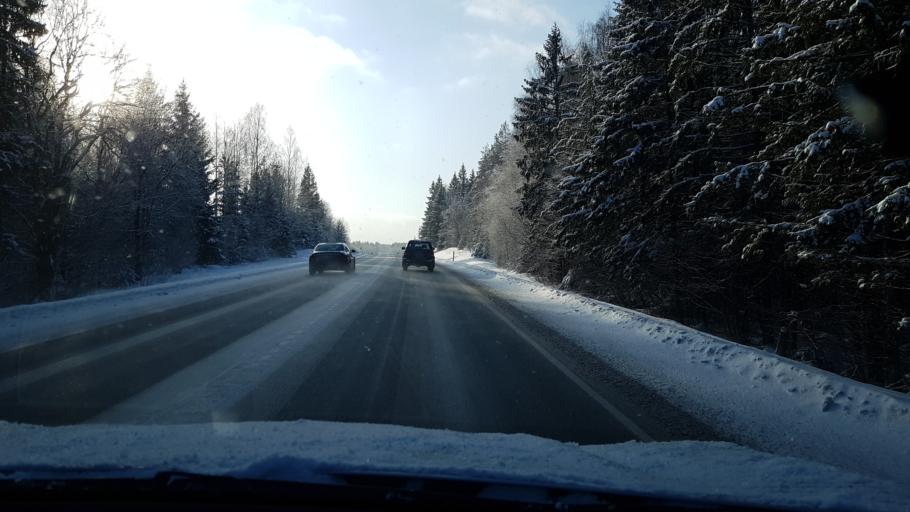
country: EE
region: Harju
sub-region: Keila linn
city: Keila
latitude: 59.2210
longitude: 24.4388
